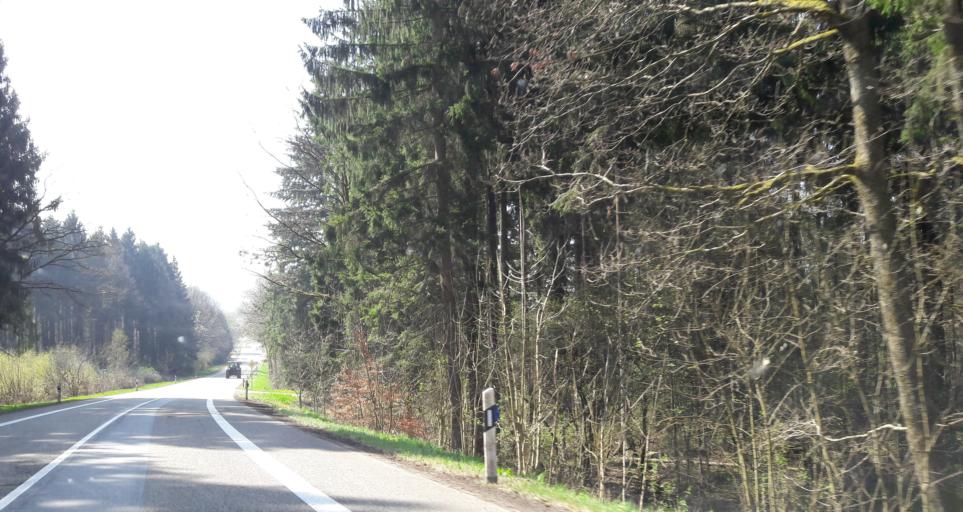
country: DE
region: Saarland
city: Tholey
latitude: 49.5076
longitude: 7.0357
